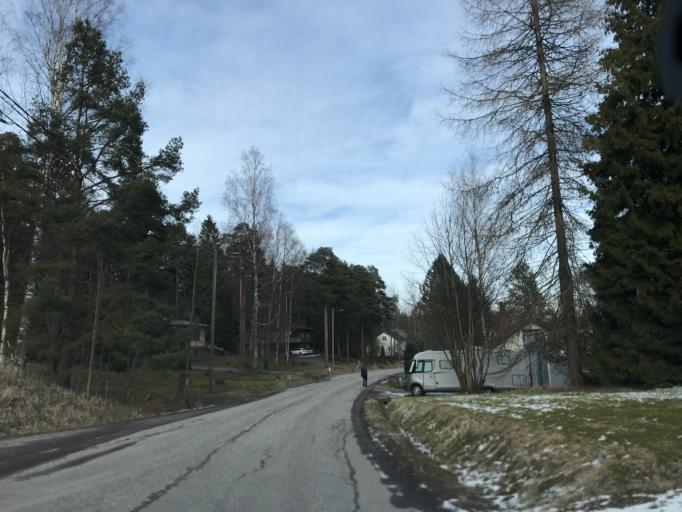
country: FI
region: Uusimaa
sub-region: Raaseporin
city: Pohja
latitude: 60.0988
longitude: 23.5408
